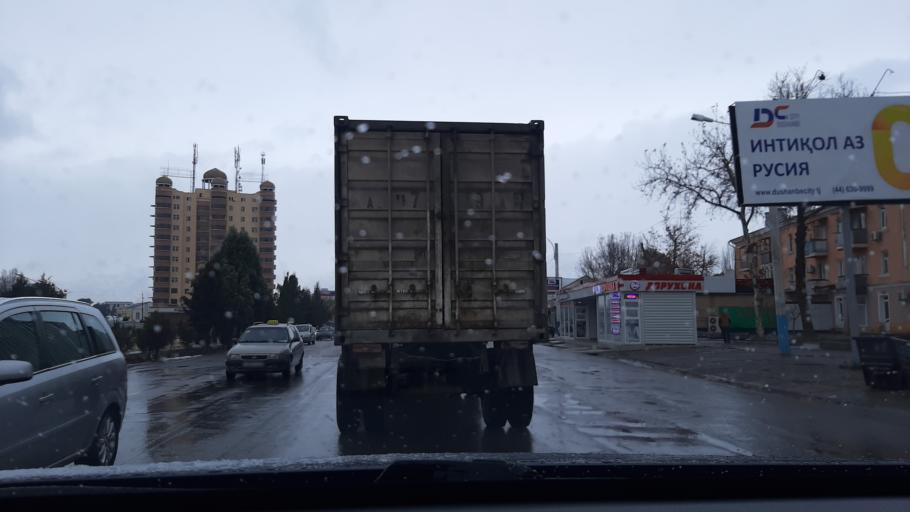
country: TJ
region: Viloyati Sughd
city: Khujand
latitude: 40.2716
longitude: 69.6439
